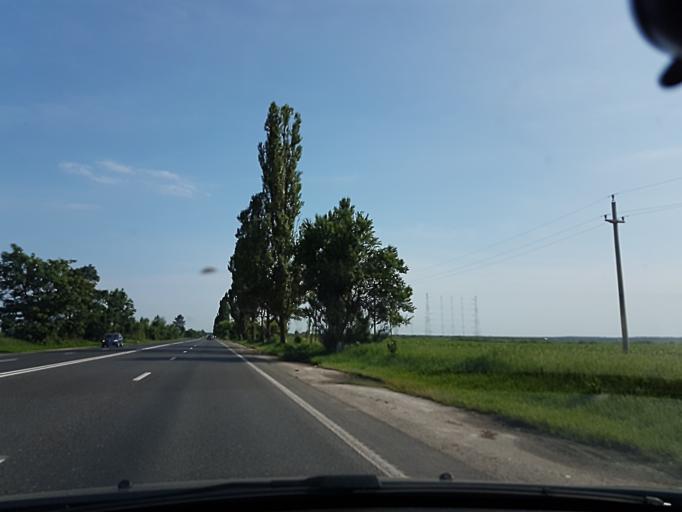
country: RO
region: Prahova
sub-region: Comuna Gorgota
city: Potigrafu
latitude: 44.7616
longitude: 26.1044
